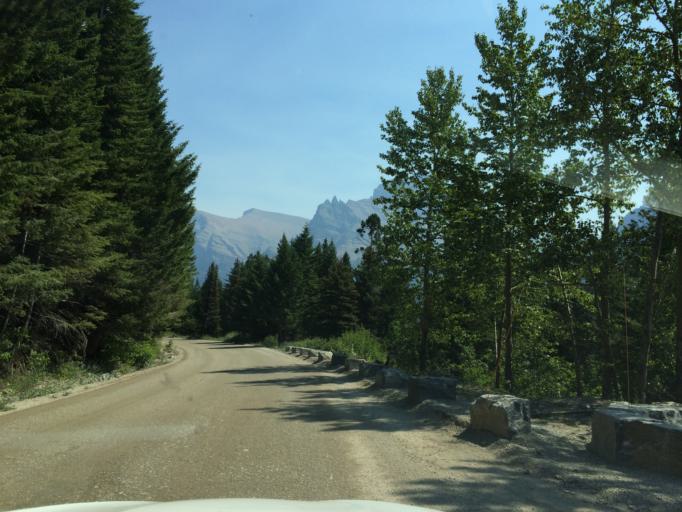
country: US
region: Montana
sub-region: Flathead County
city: Columbia Falls
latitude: 48.6776
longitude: -113.6521
